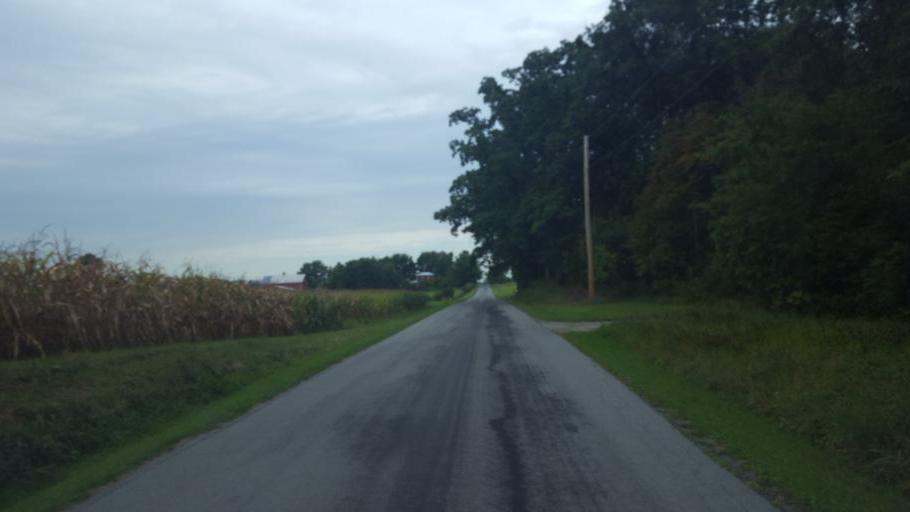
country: US
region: Ohio
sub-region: Wyandot County
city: Upper Sandusky
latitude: 40.8284
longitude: -83.1888
